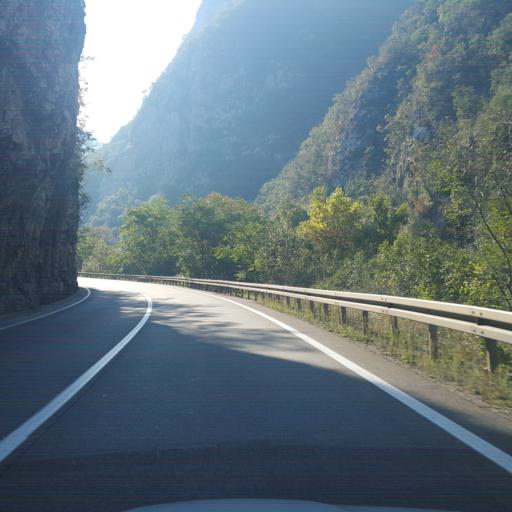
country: RS
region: Central Serbia
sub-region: Nisavski Okrug
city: Svrljig
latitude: 43.3235
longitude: 22.1661
